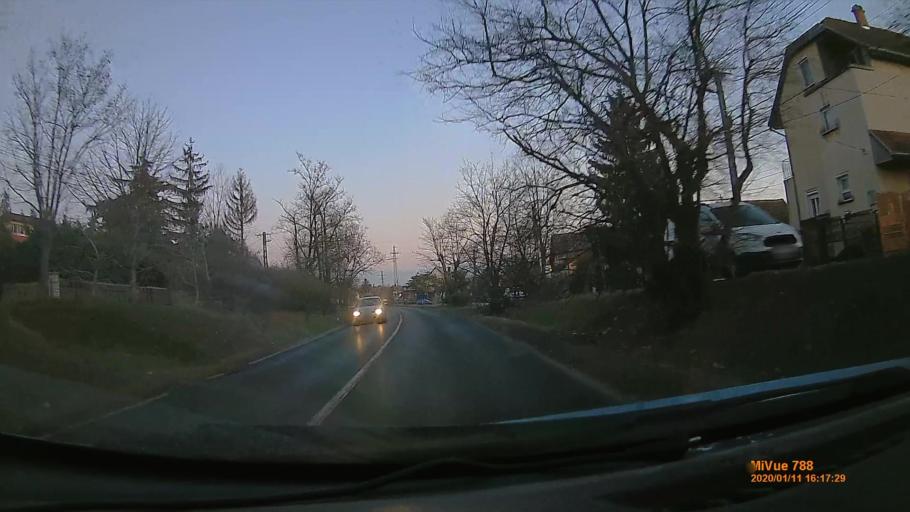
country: HU
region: Pest
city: Csomor
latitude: 47.5226
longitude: 19.2121
